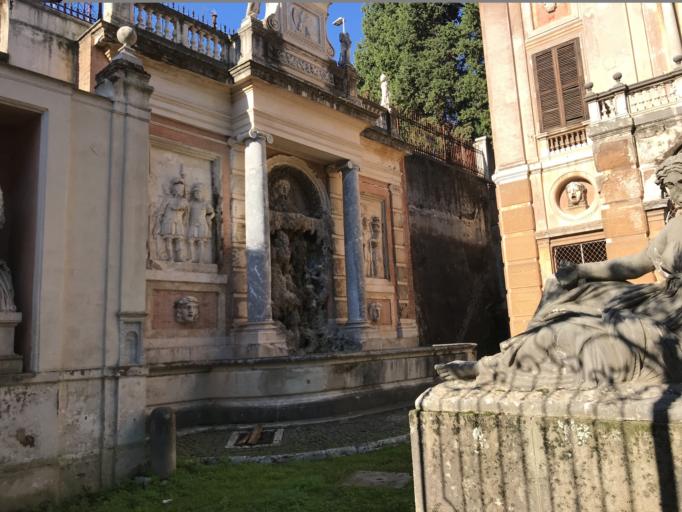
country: IT
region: Latium
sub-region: Citta metropolitana di Roma Capitale
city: Rome
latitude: 41.9143
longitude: 12.5018
